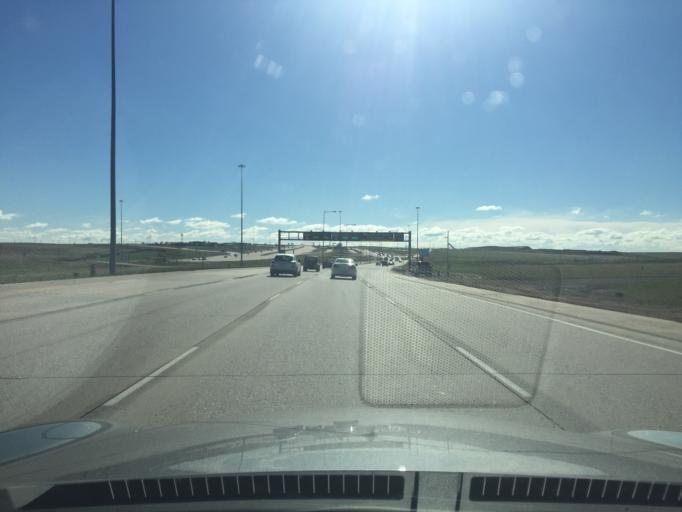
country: US
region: Colorado
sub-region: Adams County
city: Aurora
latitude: 39.8338
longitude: -104.7341
